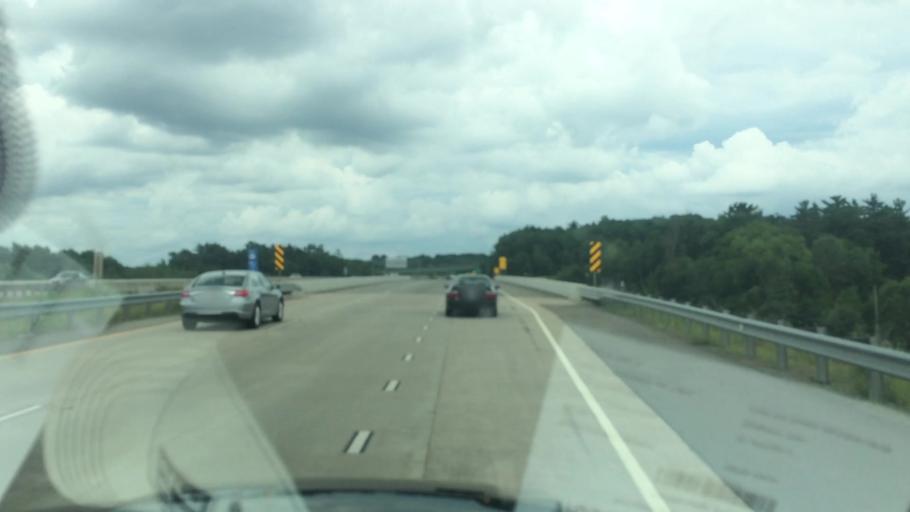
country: US
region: Wisconsin
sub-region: Marathon County
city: Rothschild
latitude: 44.8964
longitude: -89.6167
